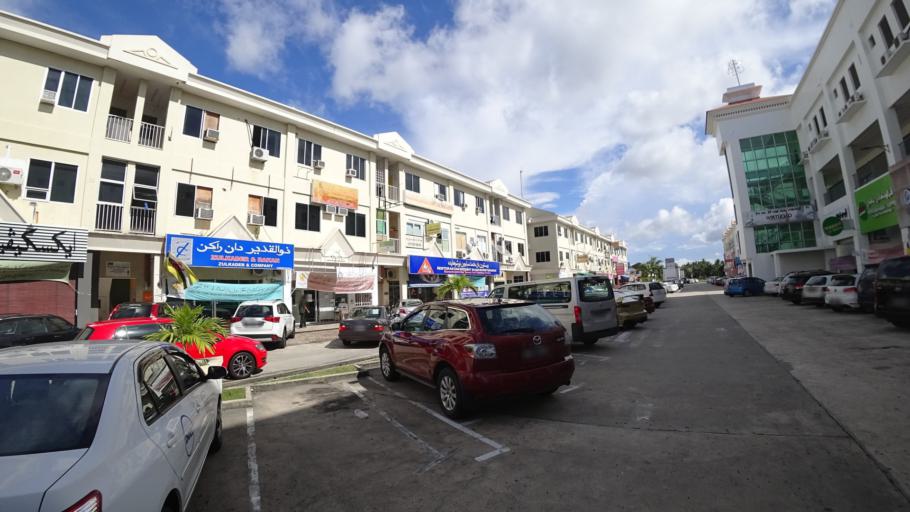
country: BN
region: Brunei and Muara
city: Bandar Seri Begawan
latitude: 4.9435
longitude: 114.9441
